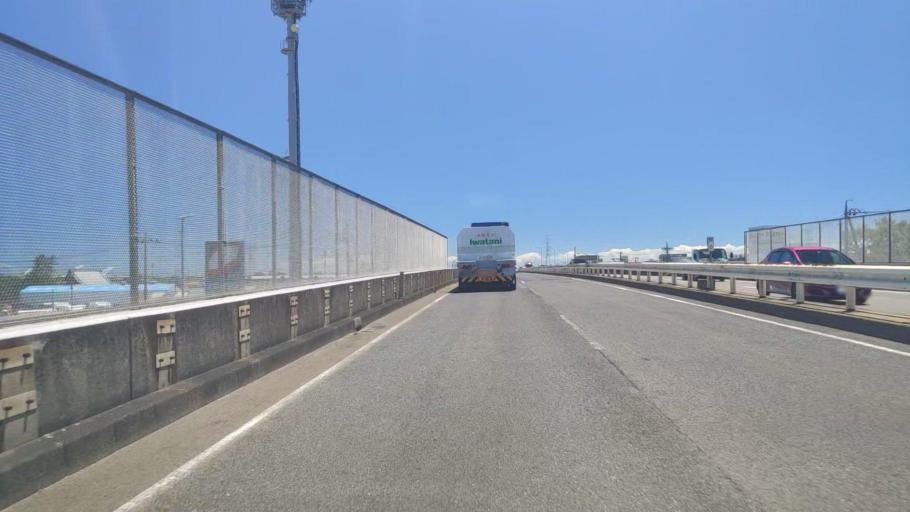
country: JP
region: Mie
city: Yokkaichi
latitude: 34.9296
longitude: 136.6154
